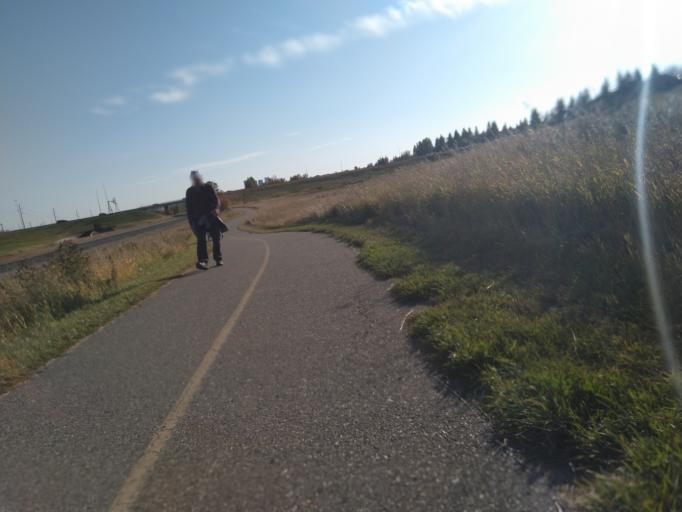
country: CA
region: Alberta
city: Calgary
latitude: 51.1138
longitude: -114.0497
